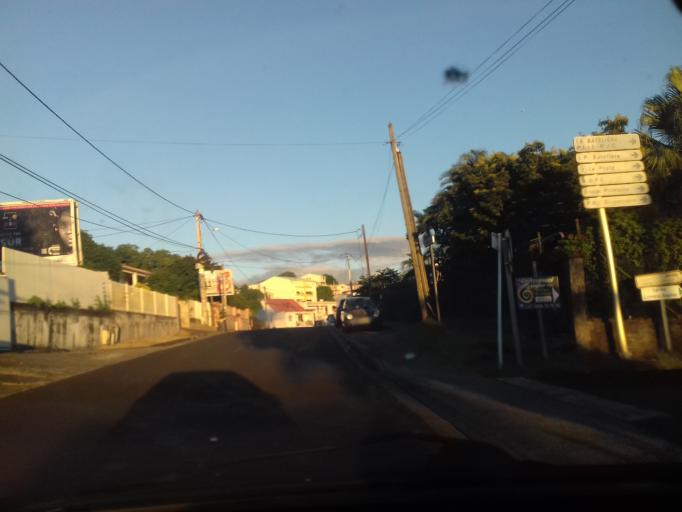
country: MQ
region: Martinique
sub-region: Martinique
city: Fort-de-France
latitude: 14.6110
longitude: -61.0947
